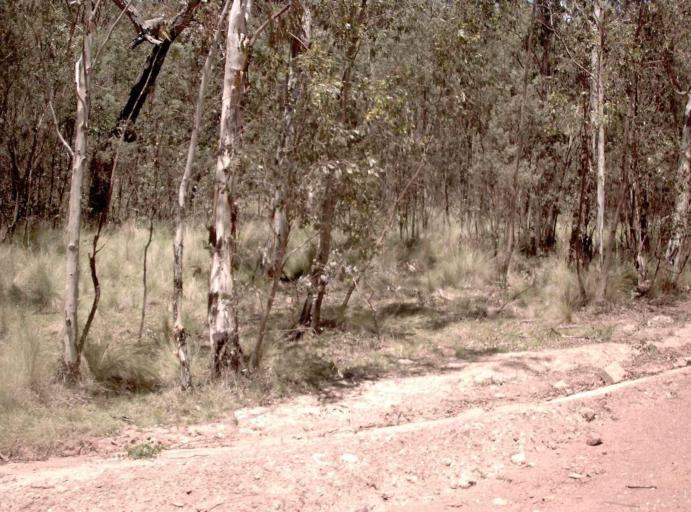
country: AU
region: New South Wales
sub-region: Snowy River
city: Jindabyne
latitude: -37.0637
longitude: 148.3182
